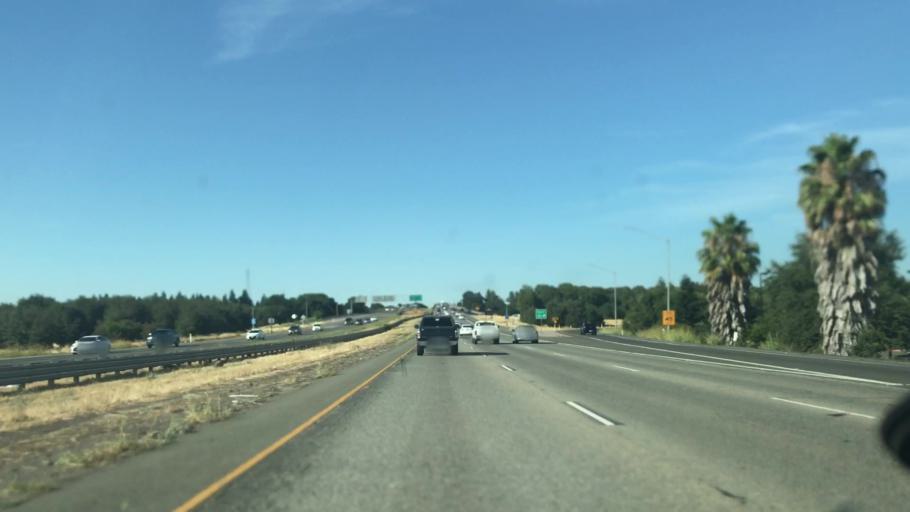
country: US
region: California
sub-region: Yolo County
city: West Sacramento
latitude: 38.5886
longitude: -121.5540
